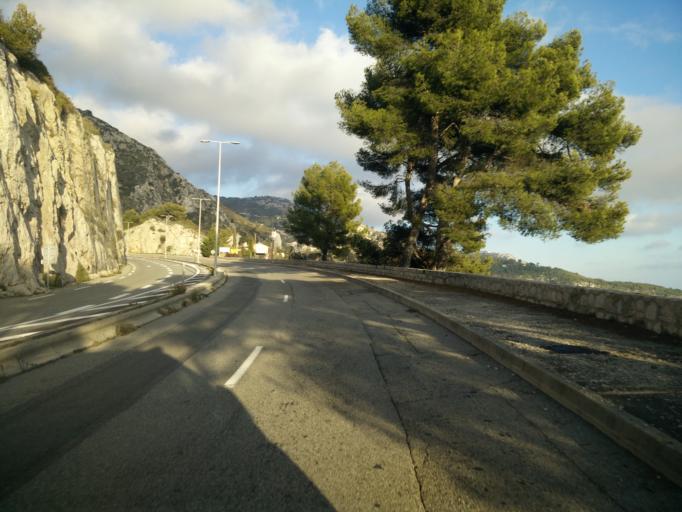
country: FR
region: Provence-Alpes-Cote d'Azur
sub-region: Departement des Alpes-Maritimes
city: Beaulieu-sur-Mer
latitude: 43.7234
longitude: 7.3464
